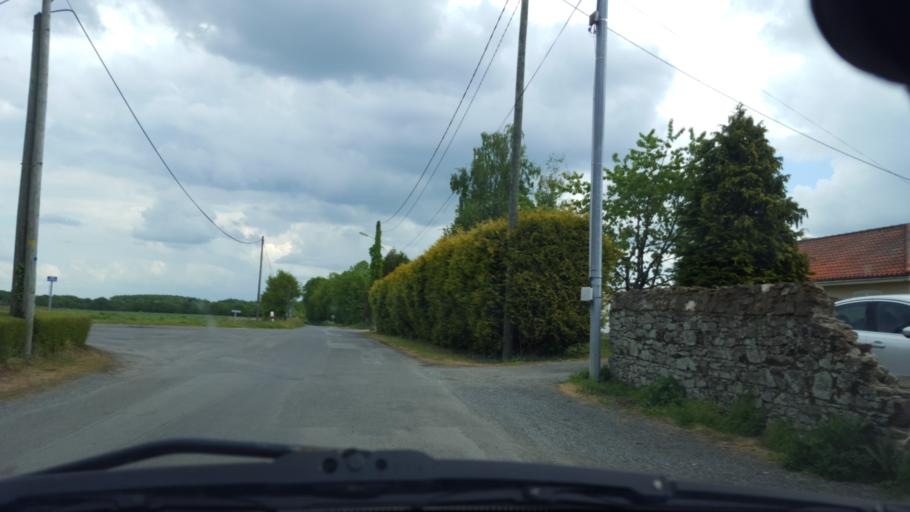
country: FR
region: Pays de la Loire
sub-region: Departement de la Loire-Atlantique
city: Saint-Philbert-de-Grand-Lieu
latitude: 47.0385
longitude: -1.6236
